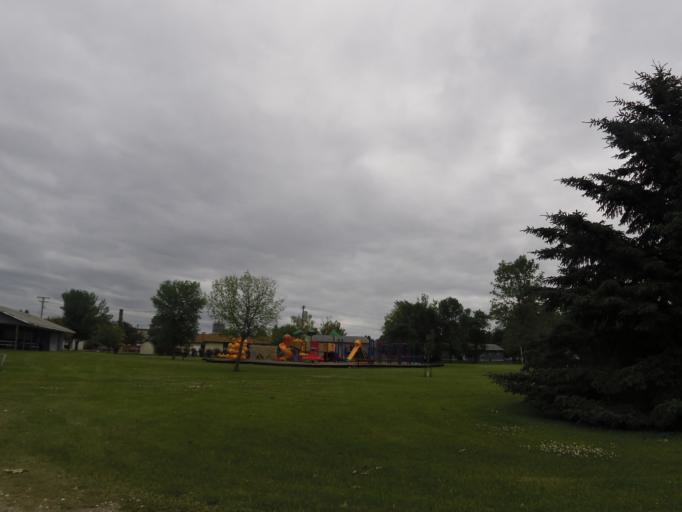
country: US
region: North Dakota
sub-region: Walsh County
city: Grafton
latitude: 48.6190
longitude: -97.4541
